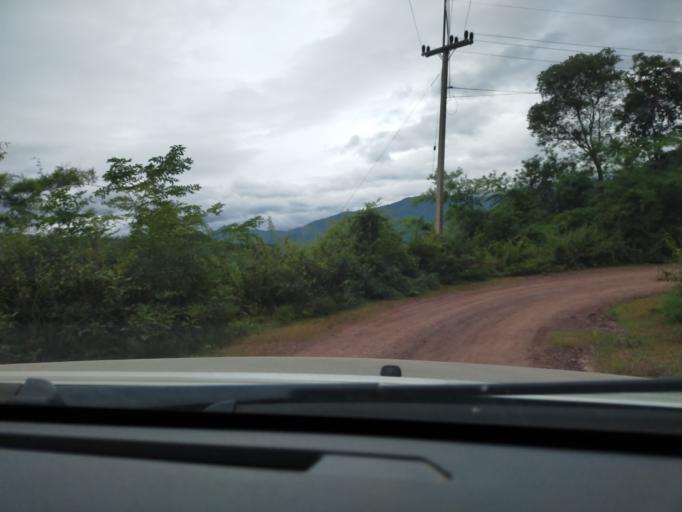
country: TH
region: Nan
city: Chaloem Phra Kiat
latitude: 19.7796
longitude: 101.3587
